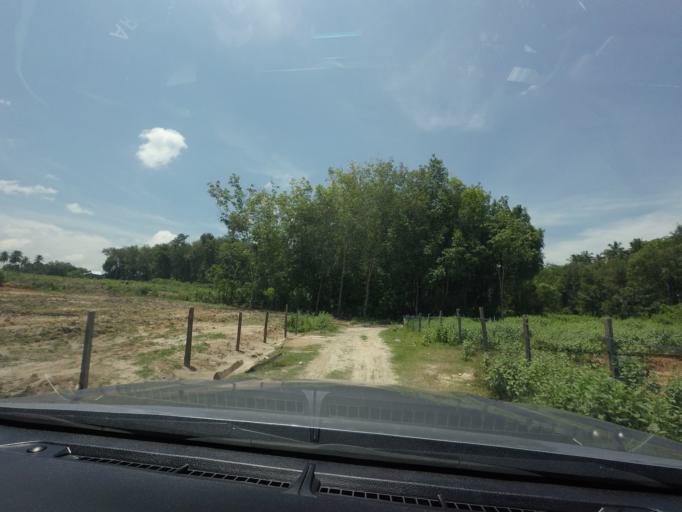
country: TH
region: Narathiwat
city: Rueso
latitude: 6.3824
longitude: 101.5131
